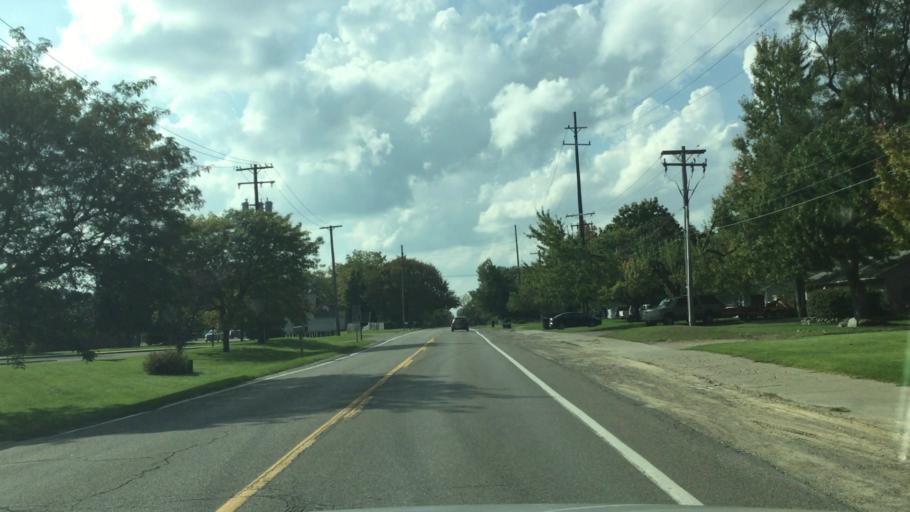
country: US
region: Michigan
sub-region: Oakland County
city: Waterford
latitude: 42.6531
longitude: -83.3884
